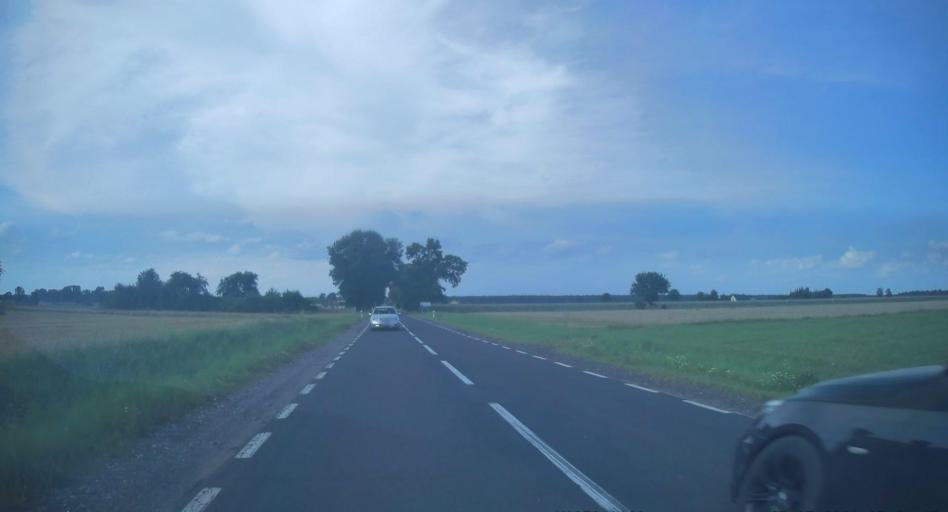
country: PL
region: Lodz Voivodeship
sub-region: Powiat tomaszowski
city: Rzeczyca
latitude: 51.6684
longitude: 20.2636
